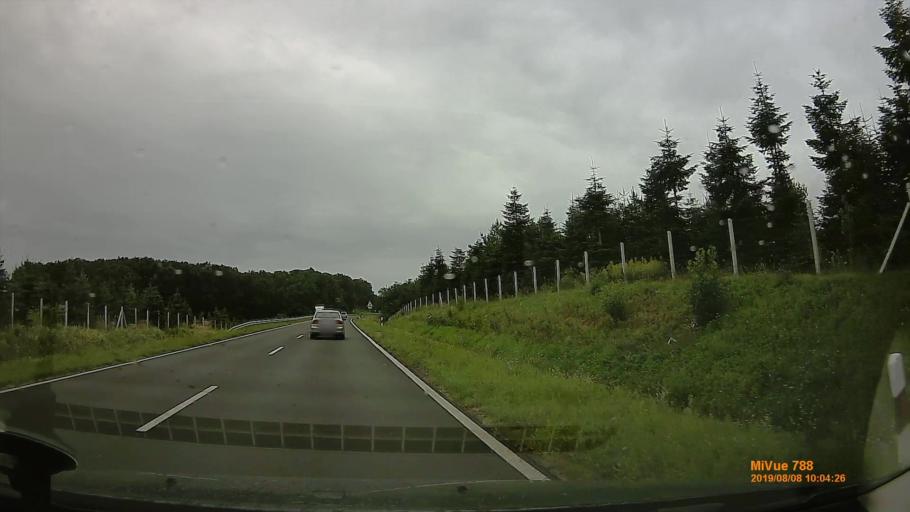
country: HU
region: Zala
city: Zalaegerszeg
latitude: 46.9146
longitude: 16.8596
